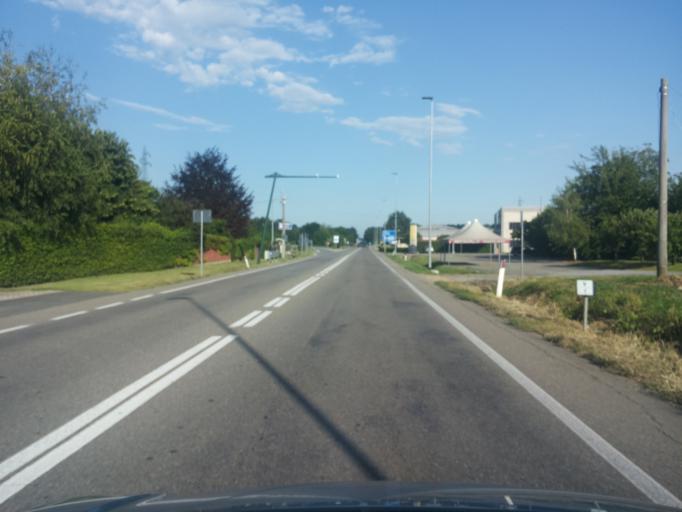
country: IT
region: Piedmont
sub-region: Provincia di Biella
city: Verrone
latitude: 45.5049
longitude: 8.1235
